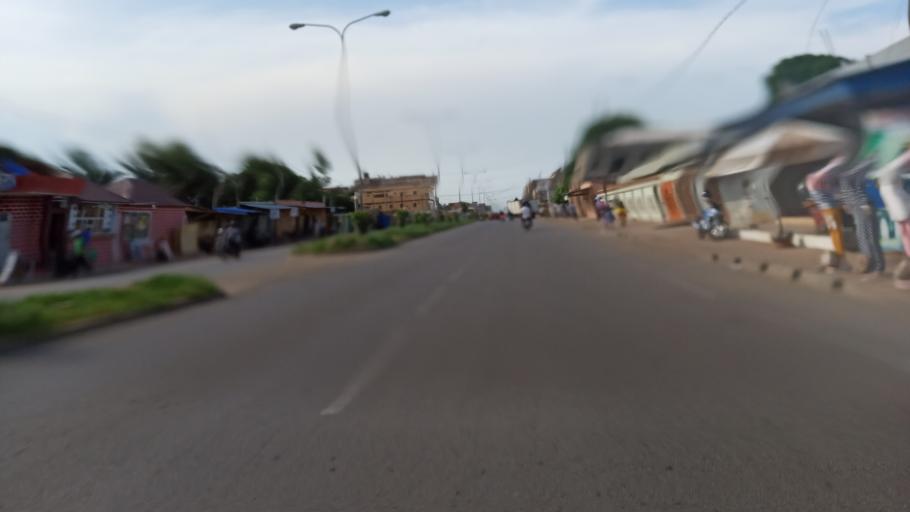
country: TG
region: Maritime
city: Lome
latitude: 6.1677
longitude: 1.2669
